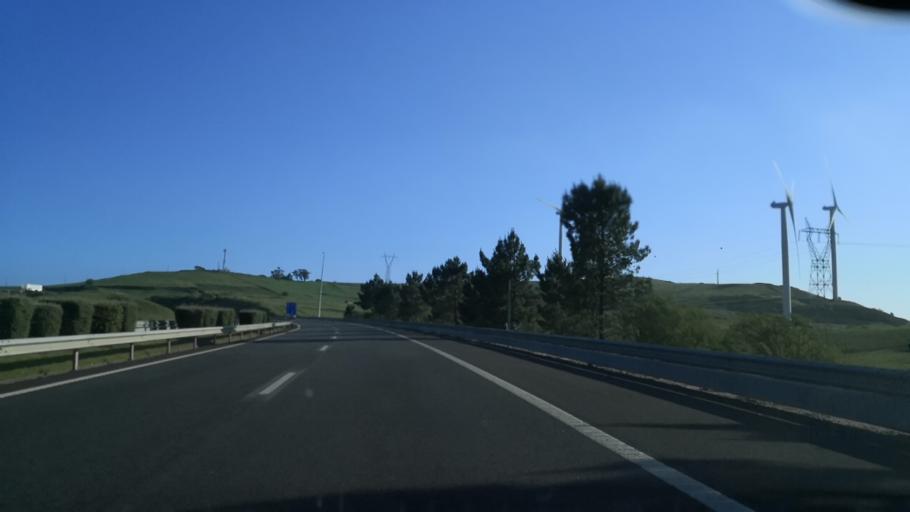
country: PT
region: Lisbon
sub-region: Mafra
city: Milharado
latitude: 38.9780
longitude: -9.2220
